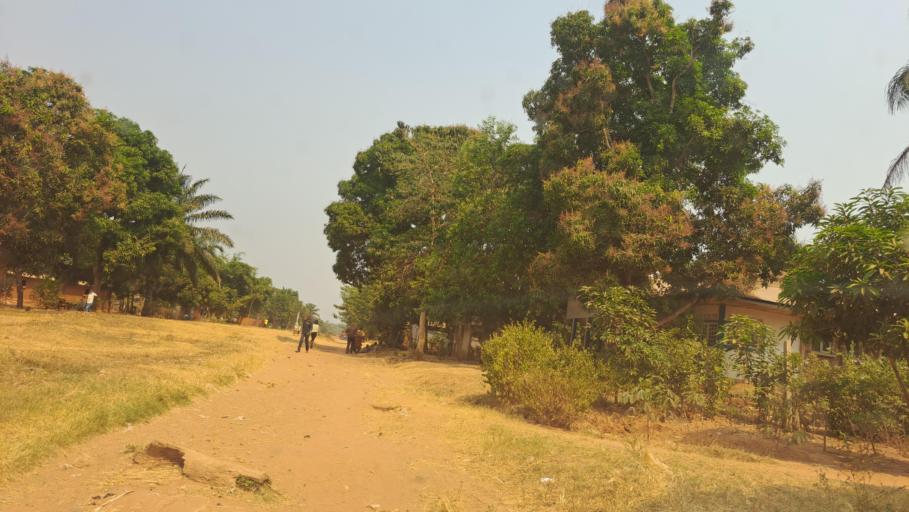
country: CD
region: Kasai-Oriental
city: Mbuji-Mayi
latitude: -6.1000
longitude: 23.5607
